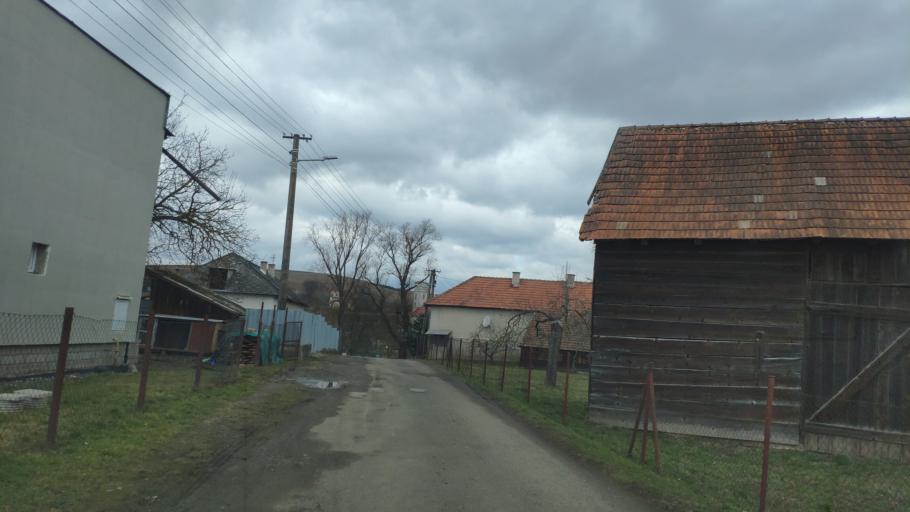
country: SK
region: Presovsky
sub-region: Okres Presov
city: Presov
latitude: 49.0879
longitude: 21.2727
